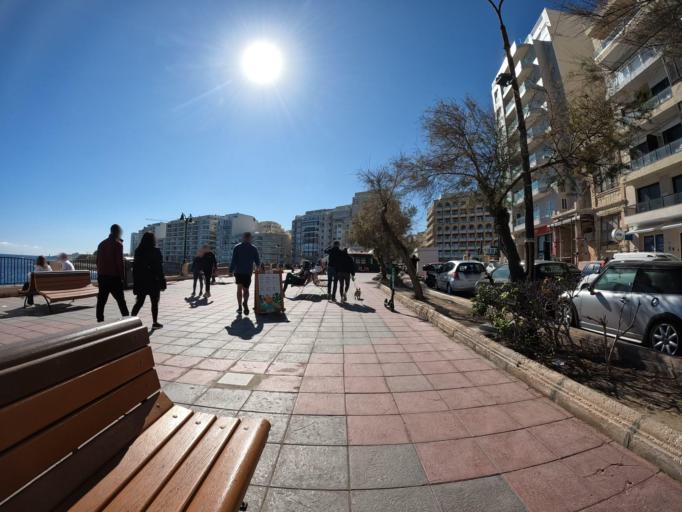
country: MT
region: Tas-Sliema
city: Sliema
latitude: 35.9129
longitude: 14.5070
